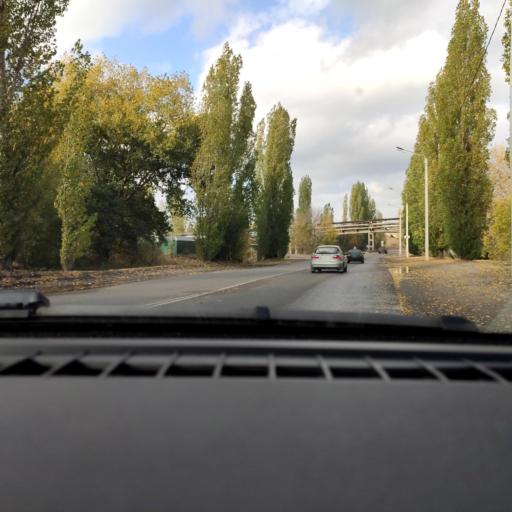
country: RU
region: Voronezj
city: Maslovka
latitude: 51.6232
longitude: 39.2611
